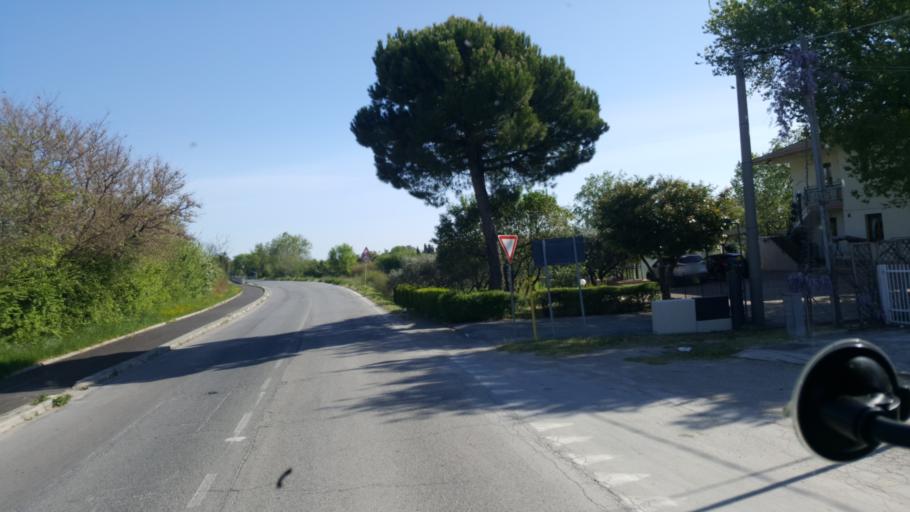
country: IT
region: Emilia-Romagna
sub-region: Provincia di Rimini
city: Poggio Berni
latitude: 44.0271
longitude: 12.4157
